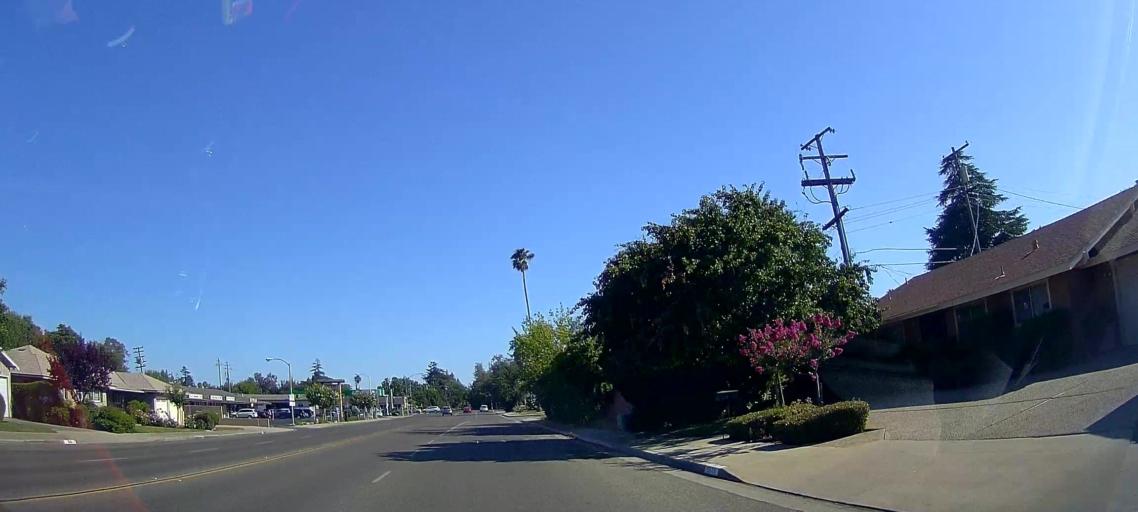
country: US
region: California
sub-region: Fresno County
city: Fresno
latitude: 36.8099
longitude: -119.7995
